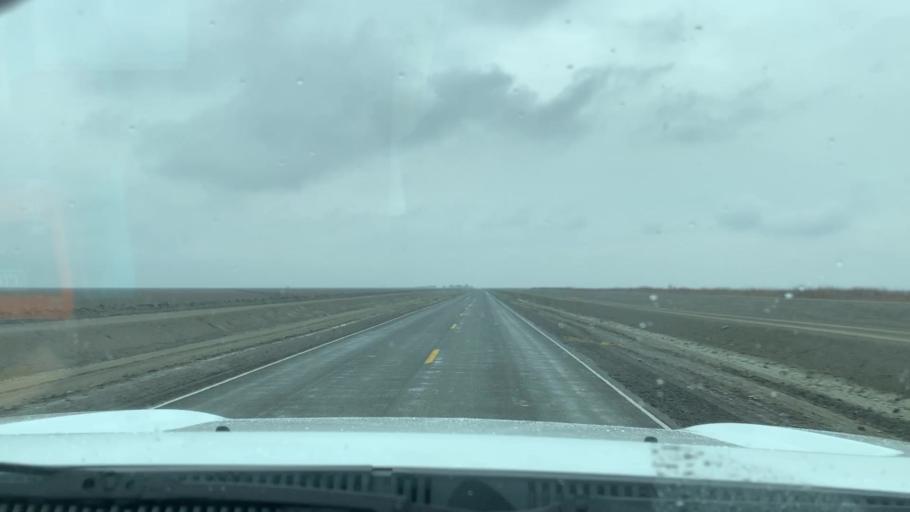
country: US
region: California
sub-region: Tulare County
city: Alpaugh
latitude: 35.9343
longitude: -119.6107
